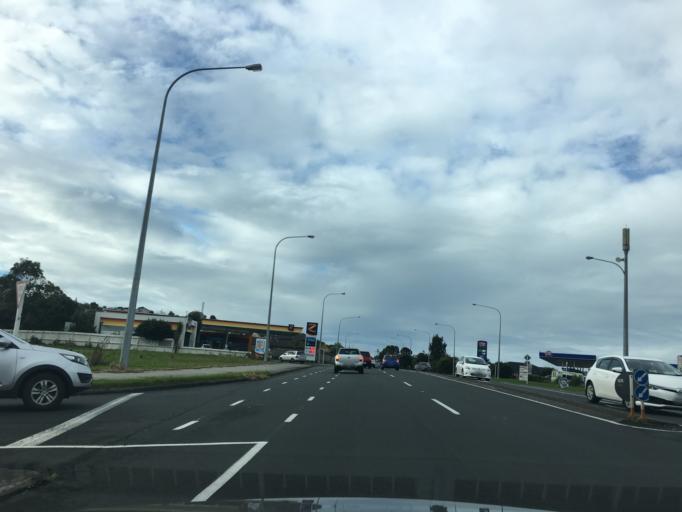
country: NZ
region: Auckland
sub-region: Auckland
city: Rothesay Bay
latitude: -36.7309
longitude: 174.7232
